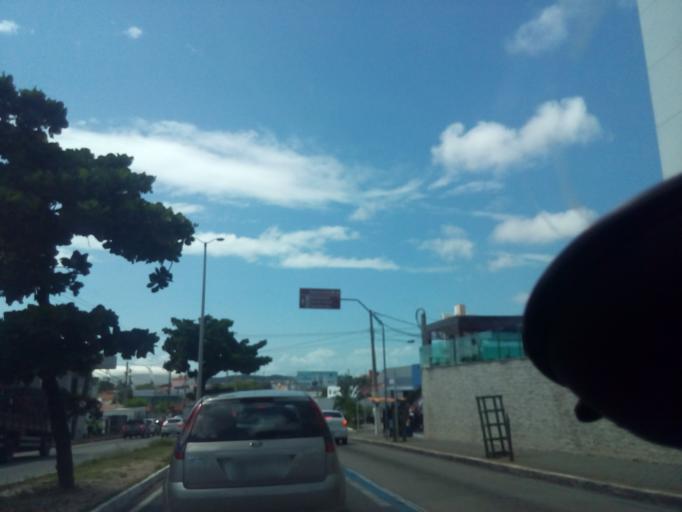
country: BR
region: Rio Grande do Norte
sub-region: Natal
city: Natal
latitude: -5.8255
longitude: -35.2218
